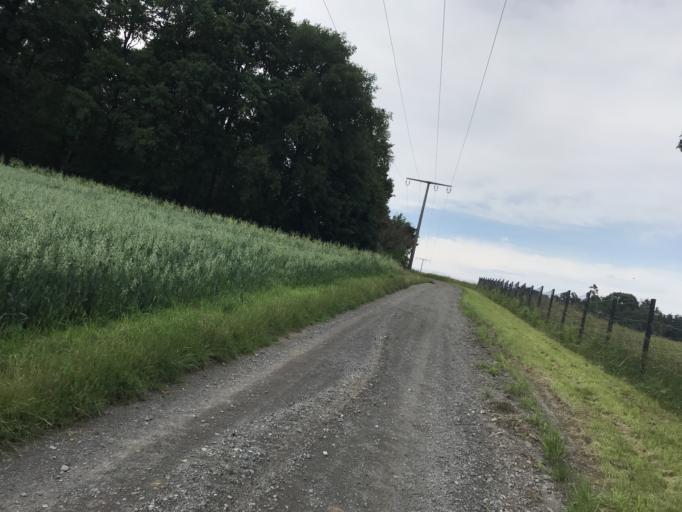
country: DE
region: Hesse
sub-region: Regierungsbezirk Giessen
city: Laubach
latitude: 50.5290
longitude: 8.9702
